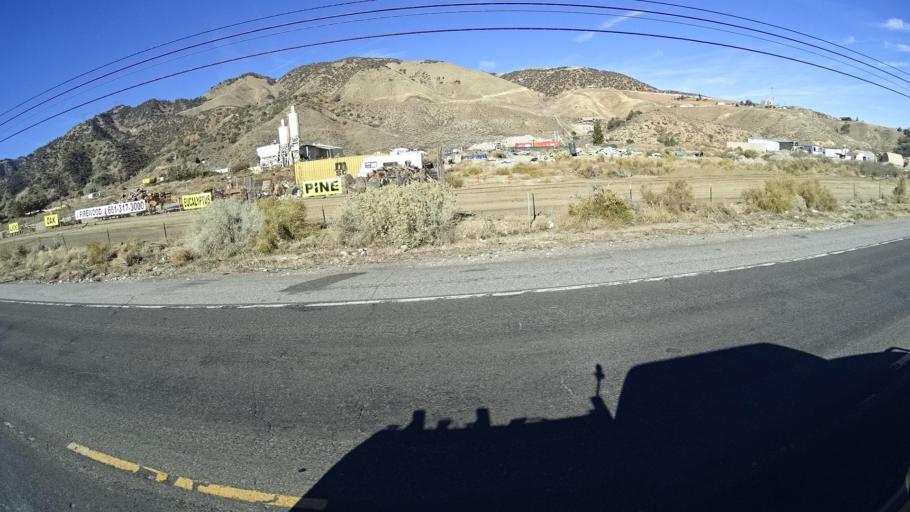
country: US
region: California
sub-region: Kern County
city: Lebec
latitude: 34.8173
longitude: -118.9011
